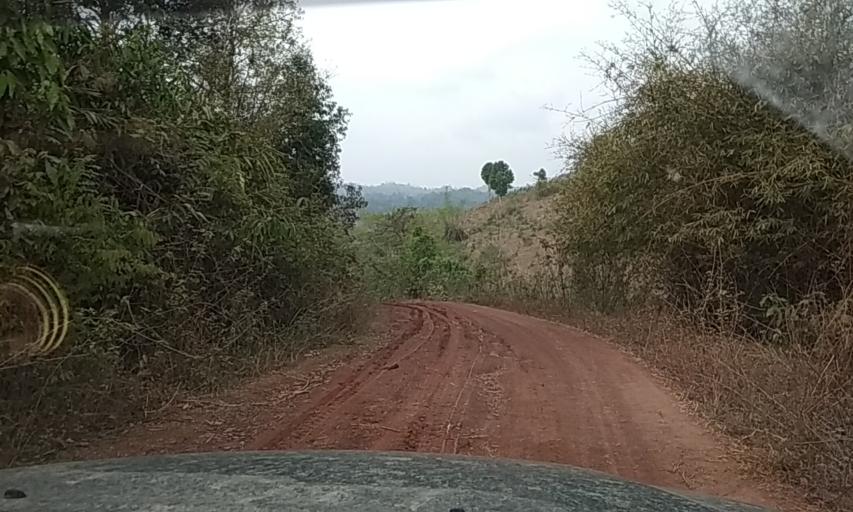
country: TH
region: Nan
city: Mae Charim
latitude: 18.4180
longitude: 101.1722
